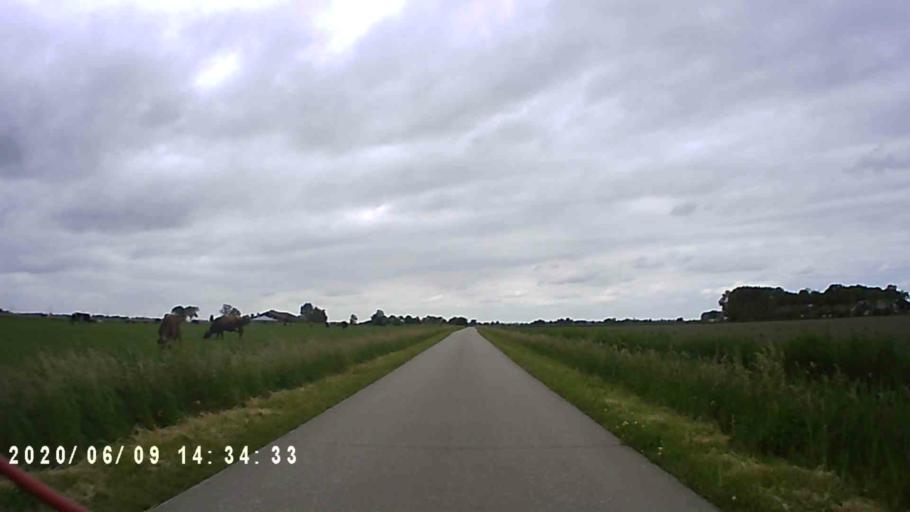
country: NL
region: Groningen
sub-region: Gemeente Bedum
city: Bedum
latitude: 53.3262
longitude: 6.5857
